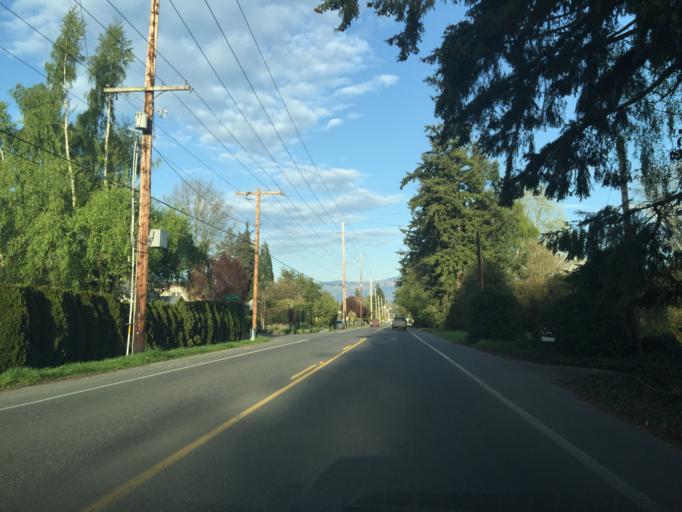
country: US
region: Washington
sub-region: Skagit County
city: Mount Vernon
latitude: 48.4207
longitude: -122.3567
